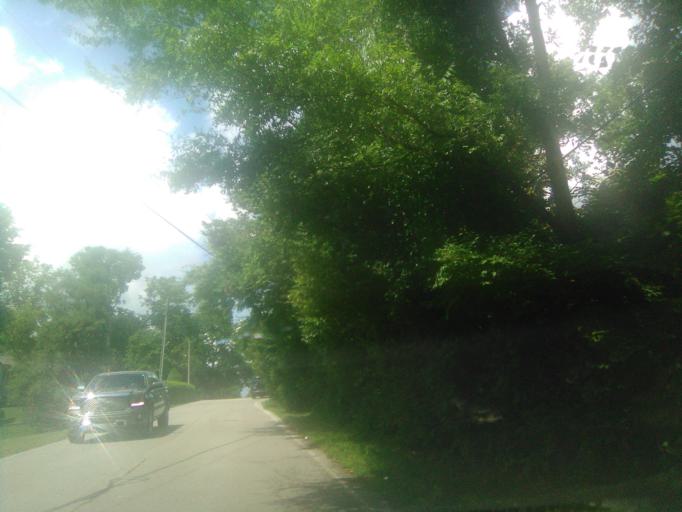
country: US
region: Tennessee
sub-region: Davidson County
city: Belle Meade
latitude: 36.1125
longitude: -86.8483
